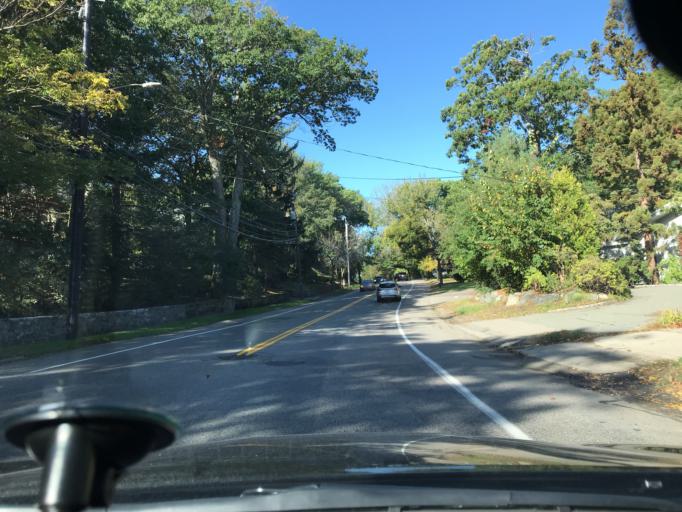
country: US
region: Massachusetts
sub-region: Suffolk County
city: Jamaica Plain
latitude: 42.3071
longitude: -71.1488
